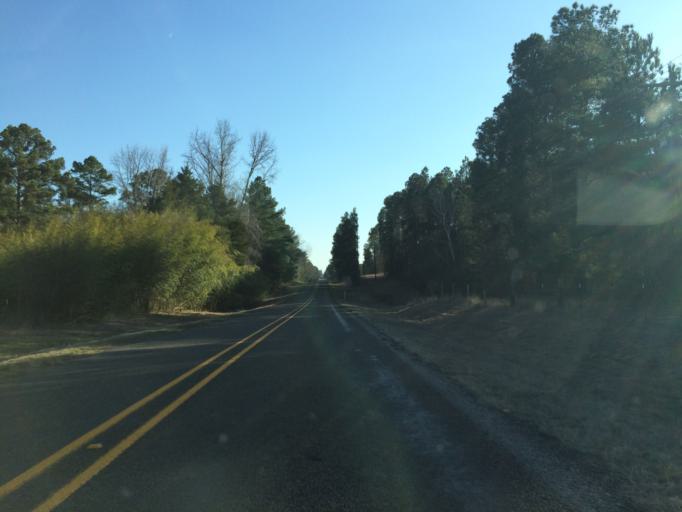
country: US
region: Texas
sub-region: Wood County
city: Hawkins
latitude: 32.6606
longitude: -95.3132
